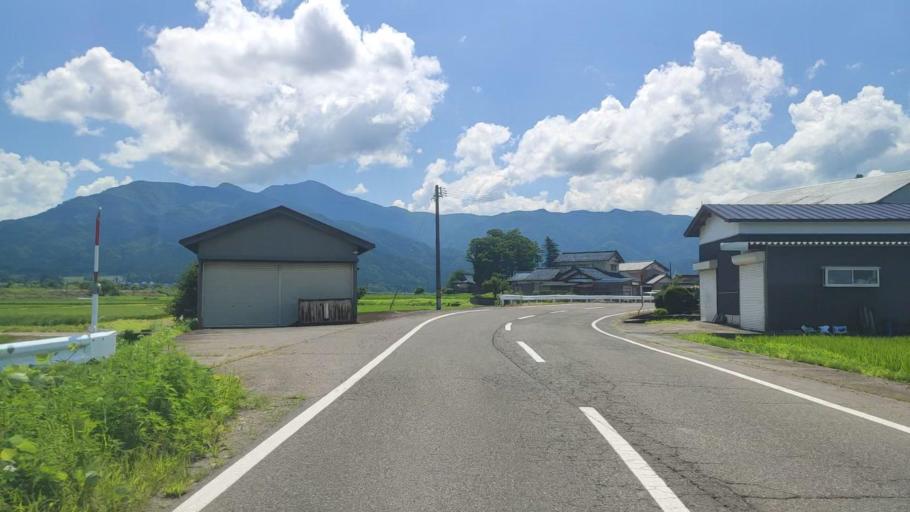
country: JP
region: Fukui
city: Ono
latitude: 35.9693
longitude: 136.5274
